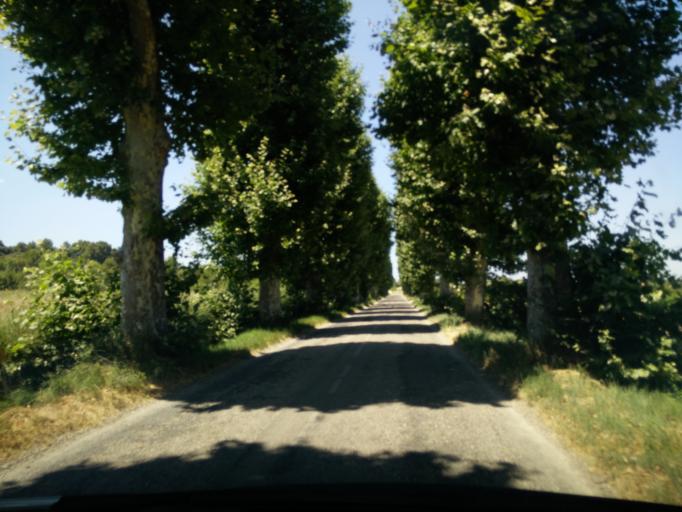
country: FR
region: Languedoc-Roussillon
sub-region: Departement de l'Herault
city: Villetelle
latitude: 43.7248
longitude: 4.1093
